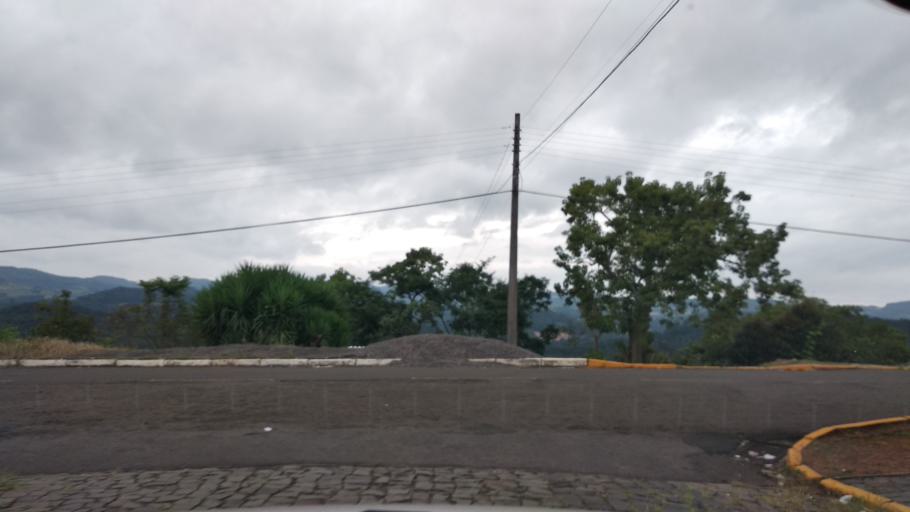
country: BR
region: Santa Catarina
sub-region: Videira
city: Videira
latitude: -26.9858
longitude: -51.1735
